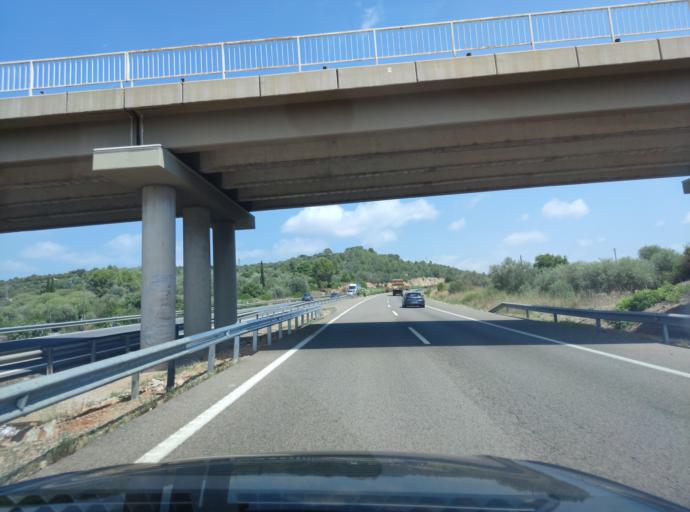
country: ES
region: Catalonia
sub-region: Provincia de Tarragona
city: Masdenverge
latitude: 40.6703
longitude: 0.5147
